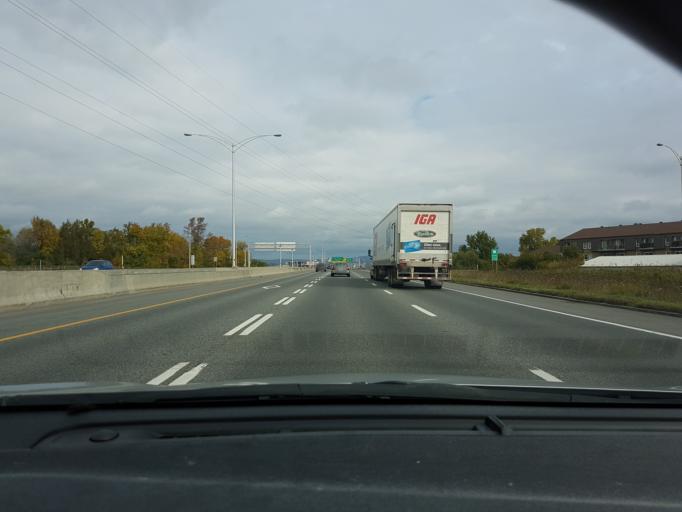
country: CA
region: Quebec
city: L'Ancienne-Lorette
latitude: 46.8083
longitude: -71.2897
